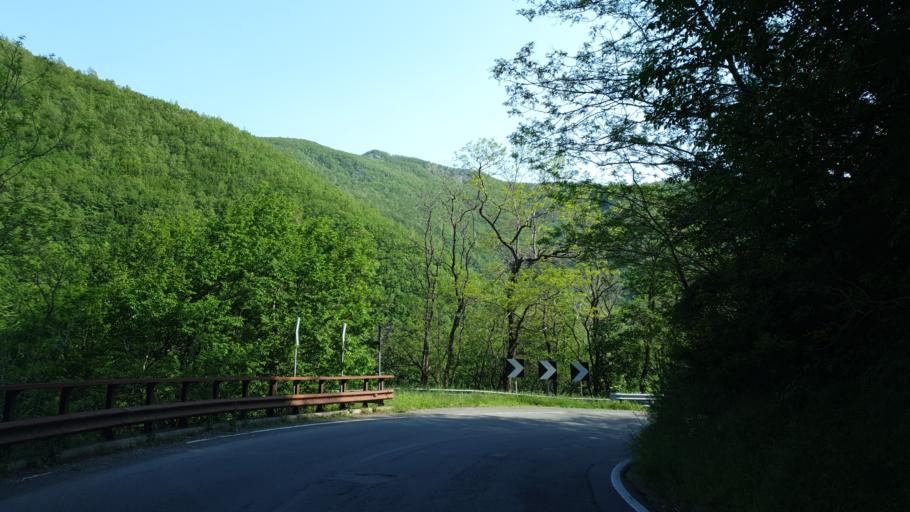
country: IT
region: Tuscany
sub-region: Province of Arezzo
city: Soci
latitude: 43.7721
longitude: 11.8660
